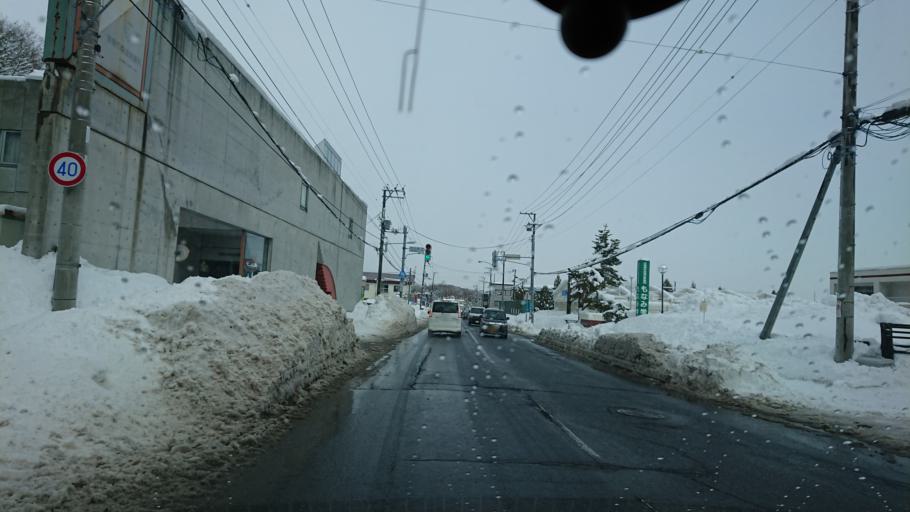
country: JP
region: Hokkaido
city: Sapporo
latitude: 42.9664
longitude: 141.3427
